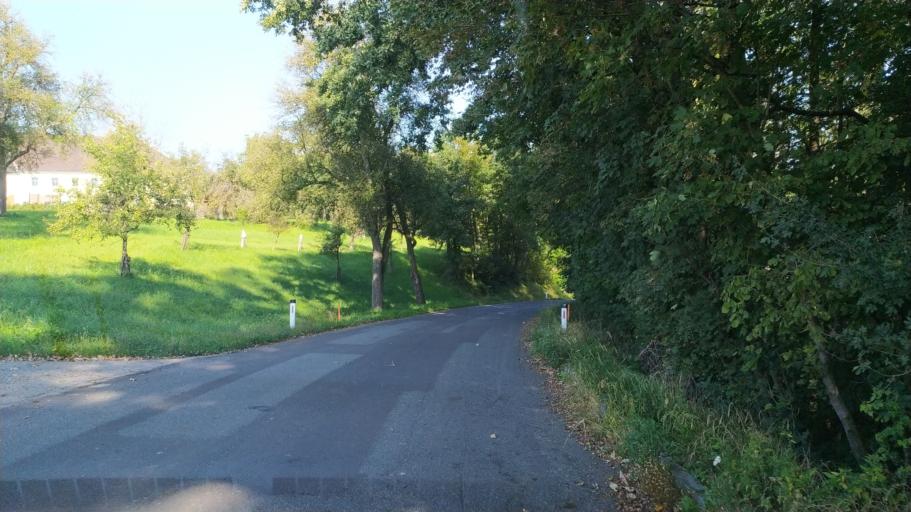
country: AT
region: Lower Austria
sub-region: Politischer Bezirk Amstetten
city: Zeillern
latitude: 48.1525
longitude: 14.7467
